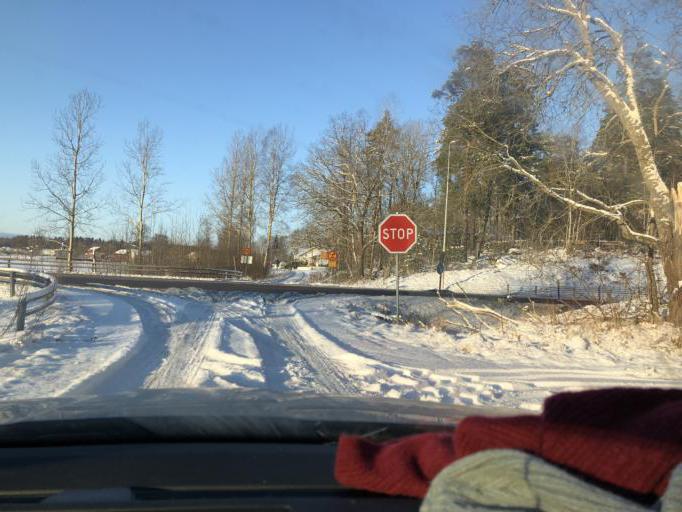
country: SE
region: Vaestra Goetaland
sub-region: Toreboda Kommun
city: Toereboda
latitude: 58.7989
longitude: 14.0609
